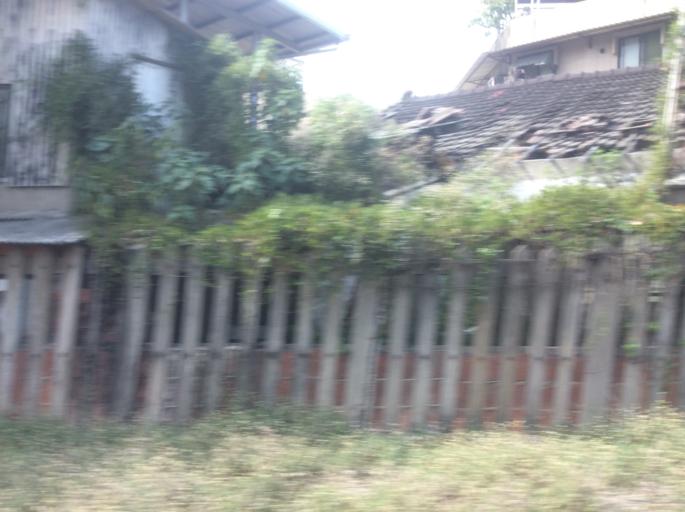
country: TW
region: Taiwan
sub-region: Tainan
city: Tainan
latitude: 22.9891
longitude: 120.2124
